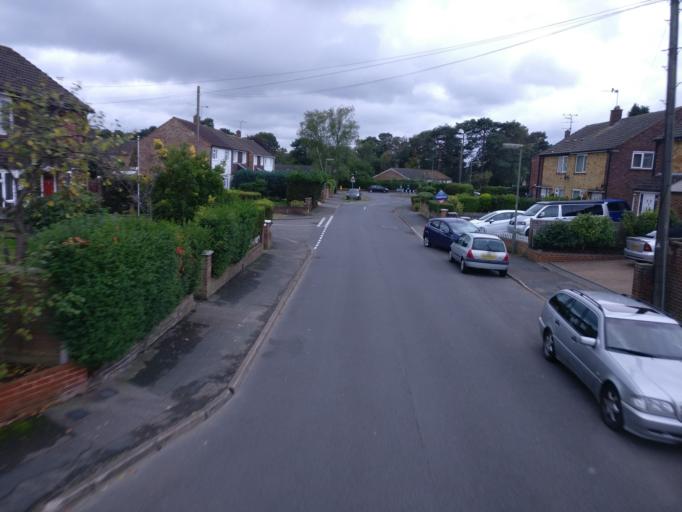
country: GB
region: England
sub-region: Surrey
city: Camberley
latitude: 51.3517
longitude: -0.7191
